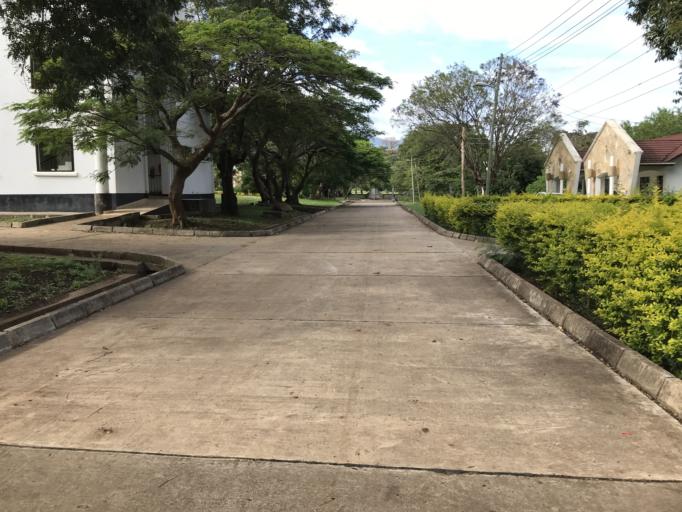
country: TZ
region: Arusha
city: Usa River
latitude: -3.3993
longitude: 36.8012
